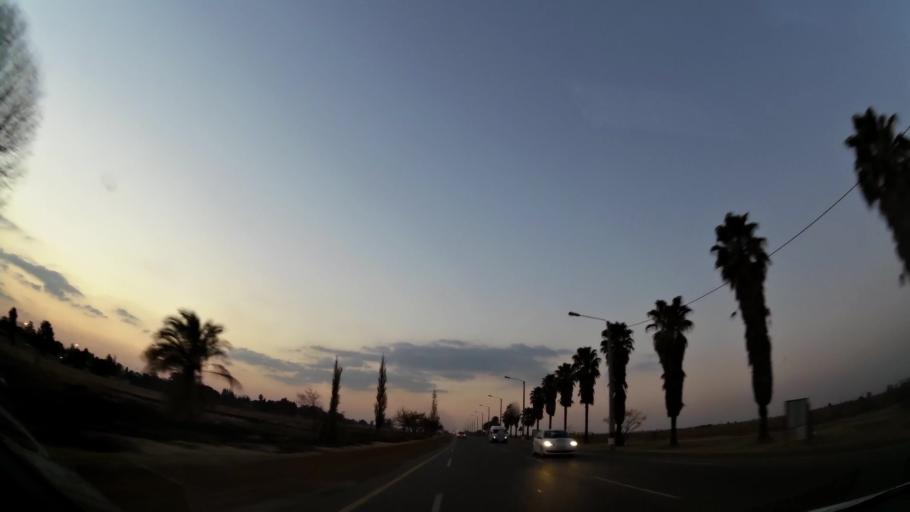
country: ZA
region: Gauteng
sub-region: Ekurhuleni Metropolitan Municipality
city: Springs
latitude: -26.3094
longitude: 28.4553
